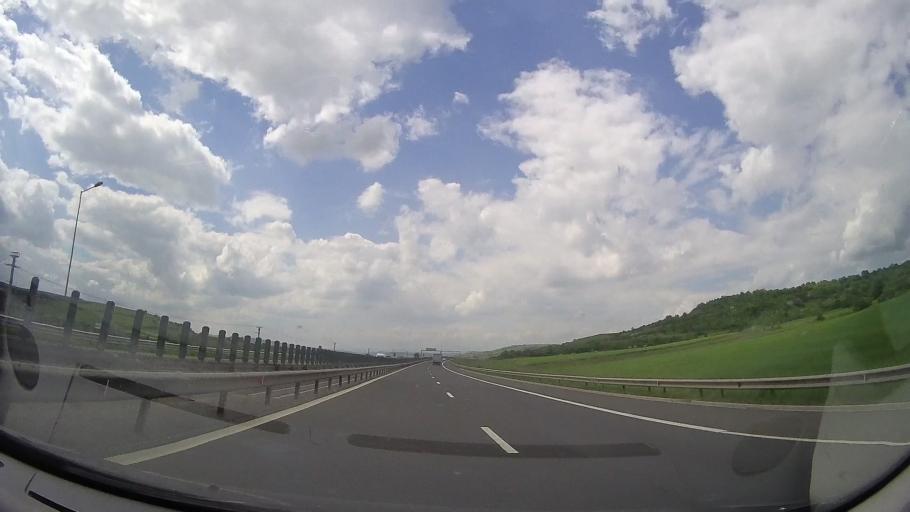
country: RO
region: Sibiu
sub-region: Comuna Apoldu de Jos
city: Apoldu de Jos
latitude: 45.8769
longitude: 23.8667
